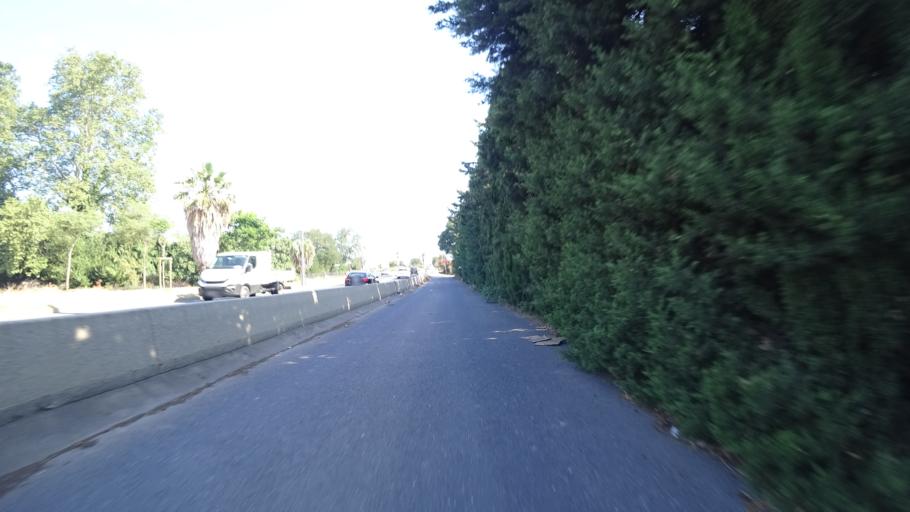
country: FR
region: Languedoc-Roussillon
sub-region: Departement des Pyrenees-Orientales
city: Perpignan
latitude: 42.7061
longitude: 2.9092
